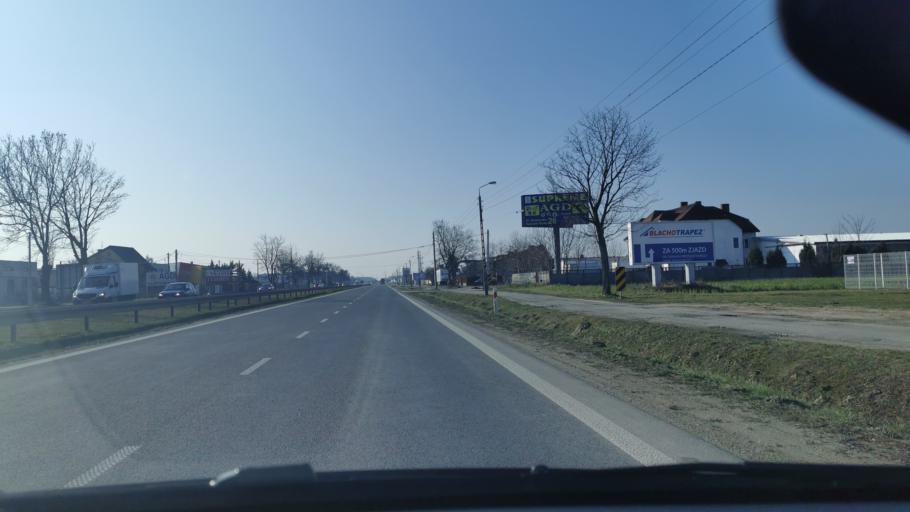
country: PL
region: Masovian Voivodeship
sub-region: Powiat pruszkowski
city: Nowe Grocholice
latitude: 52.1209
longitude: 20.8934
